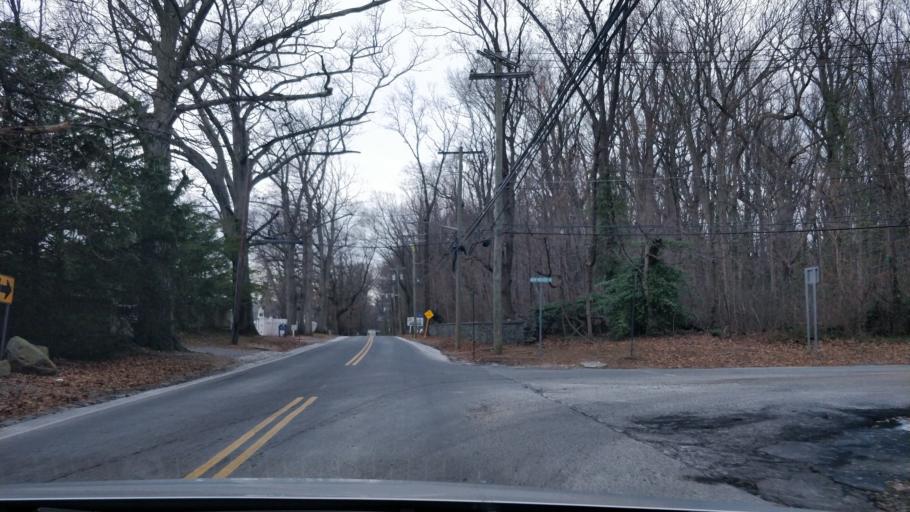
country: US
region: New York
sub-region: Nassau County
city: Glen Cove
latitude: 40.8779
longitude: -73.6415
